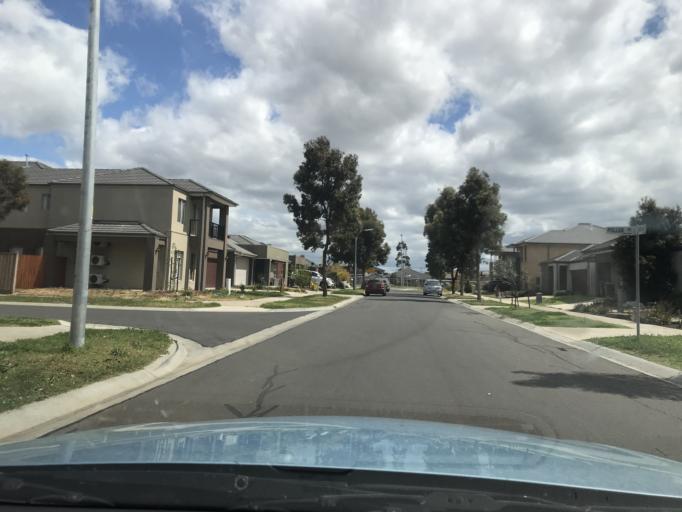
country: AU
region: Victoria
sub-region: Wyndham
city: Williams Landing
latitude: -37.8578
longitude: 144.7494
